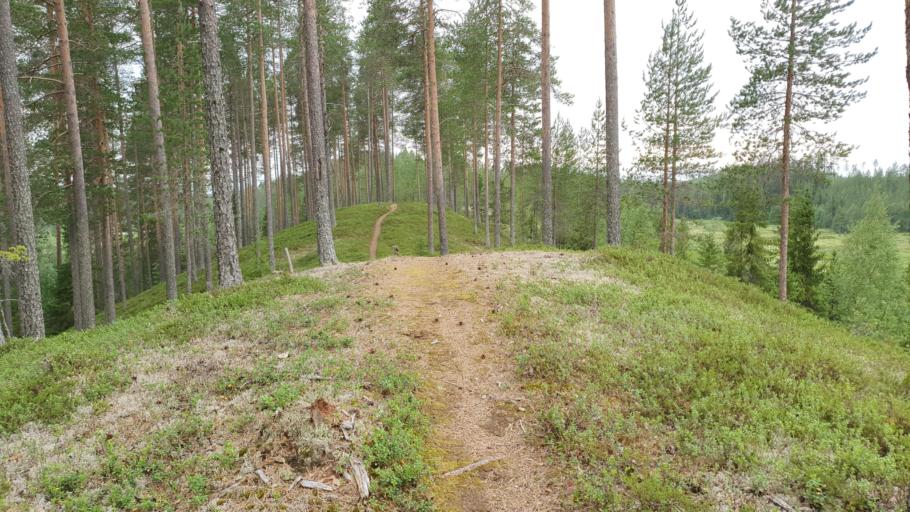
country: RU
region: Republic of Karelia
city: Kostomuksha
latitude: 64.7568
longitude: 29.9975
